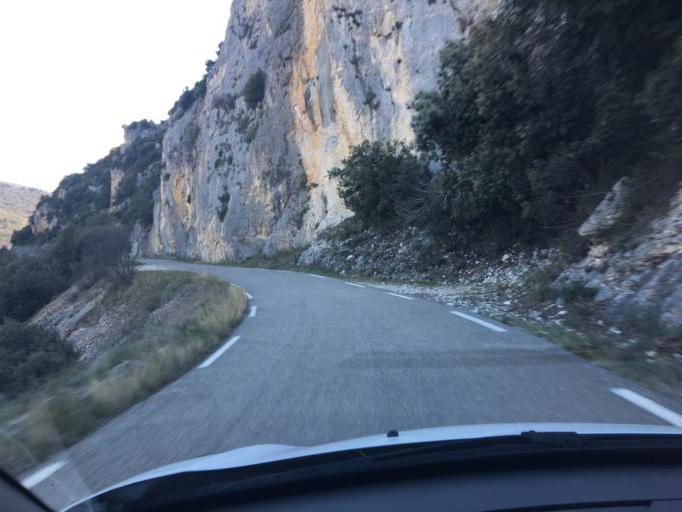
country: FR
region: Provence-Alpes-Cote d'Azur
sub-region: Departement du Vaucluse
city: Villes-sur-Auzon
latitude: 44.0641
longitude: 5.3024
